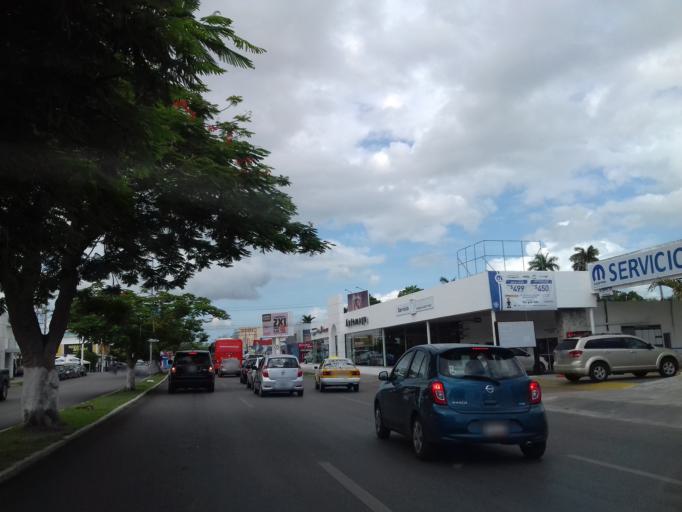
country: MX
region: Yucatan
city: Merida
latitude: 20.9922
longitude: -89.6164
